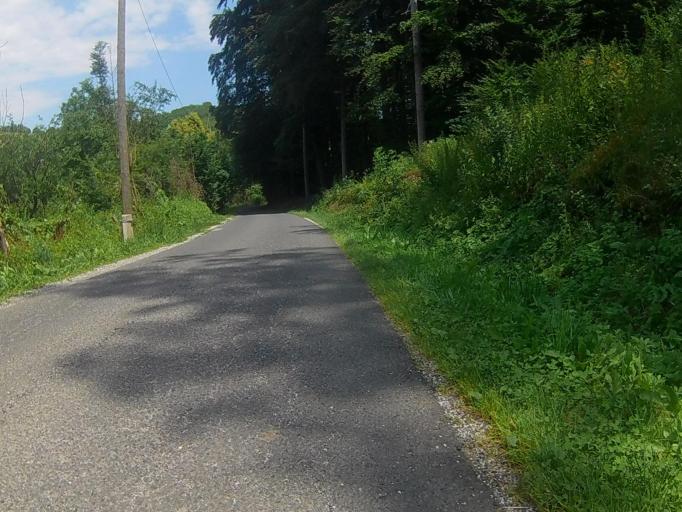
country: SI
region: Maribor
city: Kamnica
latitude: 46.5911
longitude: 15.6256
